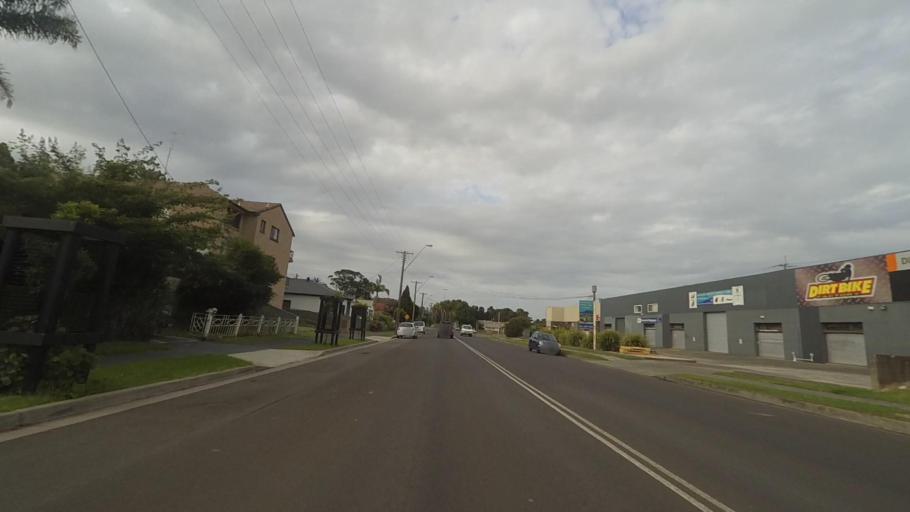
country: AU
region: New South Wales
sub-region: Wollongong
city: Wollongong
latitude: -34.4231
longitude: 150.8882
